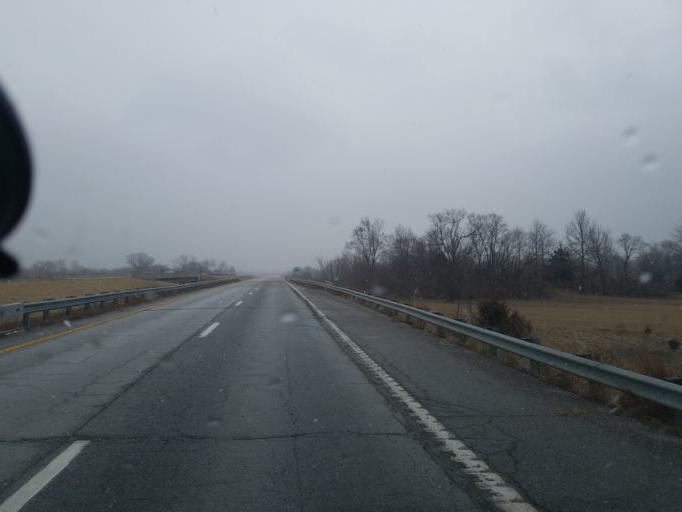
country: US
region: Missouri
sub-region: Macon County
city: La Plata
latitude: 40.0318
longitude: -92.4866
